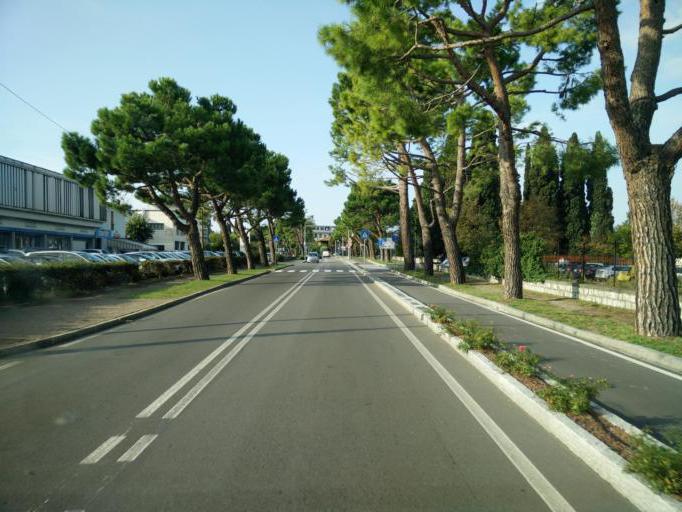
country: IT
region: Lombardy
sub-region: Provincia di Brescia
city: Iseo
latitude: 45.6626
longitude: 10.0573
